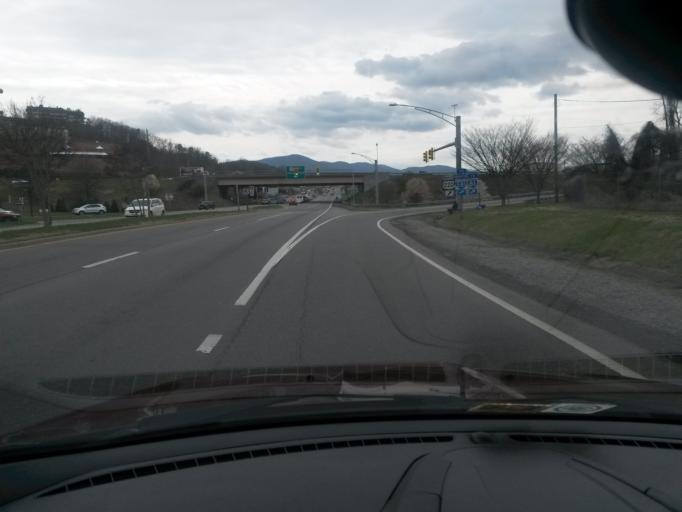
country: US
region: Virginia
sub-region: Roanoke County
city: Narrows
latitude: 37.2332
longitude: -79.9720
